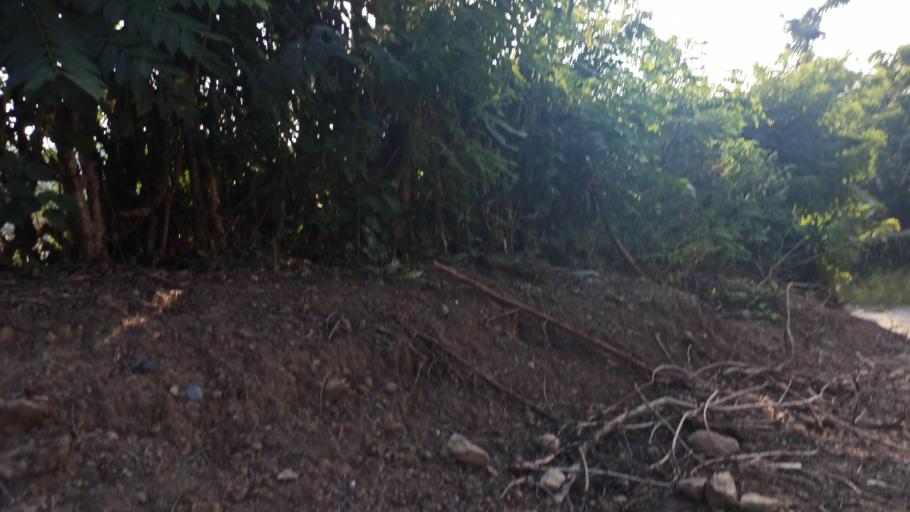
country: MX
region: Veracruz
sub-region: Papantla
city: Polutla
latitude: 20.6007
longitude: -97.2593
